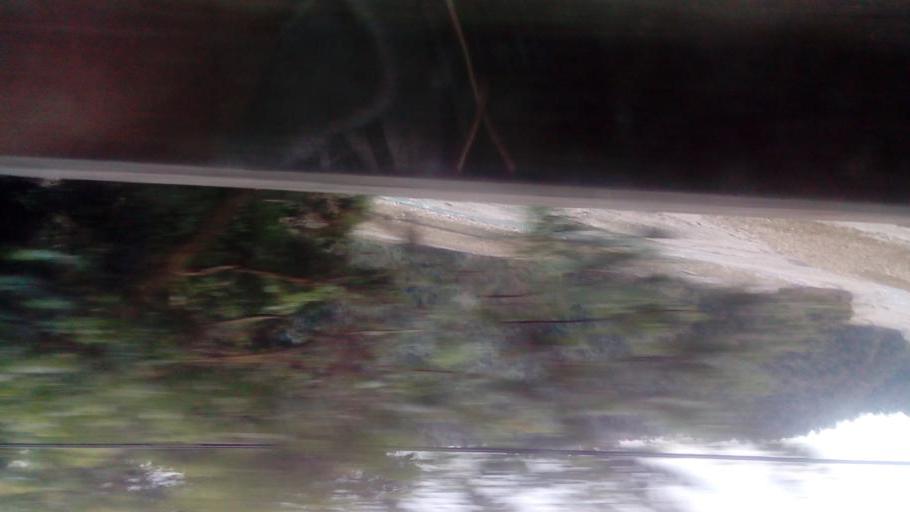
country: TW
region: Taiwan
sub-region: Yilan
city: Yilan
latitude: 24.6362
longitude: 121.5540
